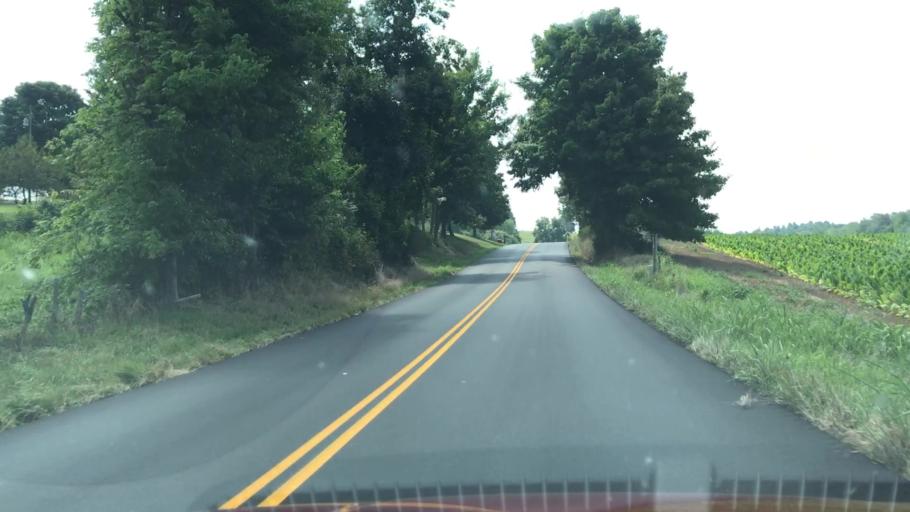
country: US
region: Kentucky
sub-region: Monroe County
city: Tompkinsville
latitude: 36.7638
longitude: -85.7962
